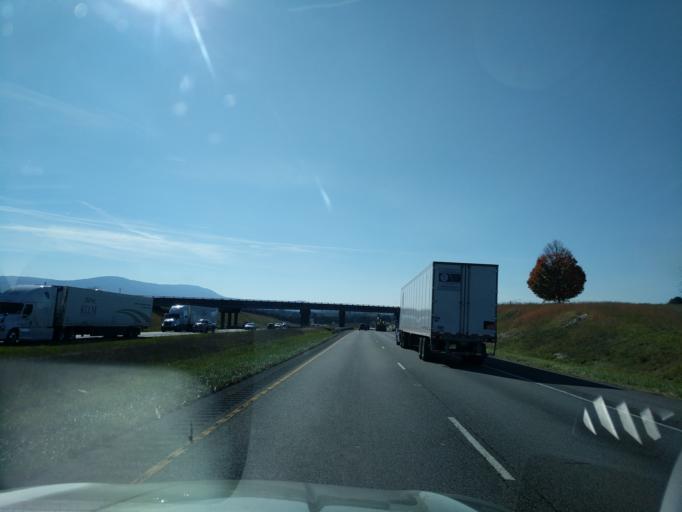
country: US
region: Virginia
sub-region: Rockingham County
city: Broadway
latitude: 38.5648
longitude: -78.7444
